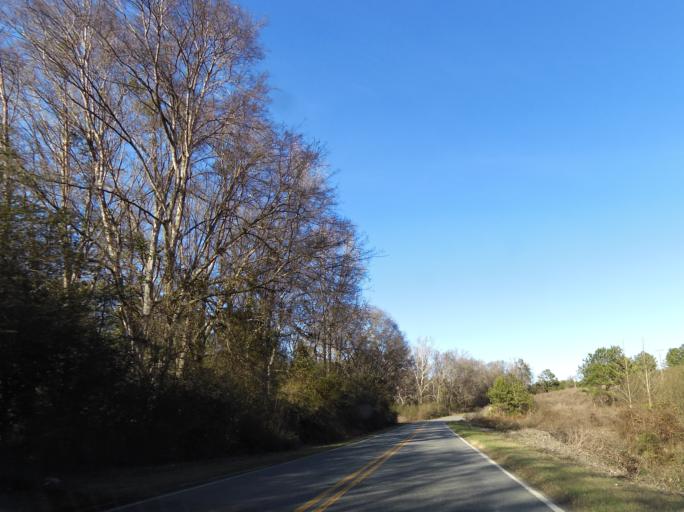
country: US
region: Georgia
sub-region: Bibb County
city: West Point
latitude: 32.7661
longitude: -83.8383
